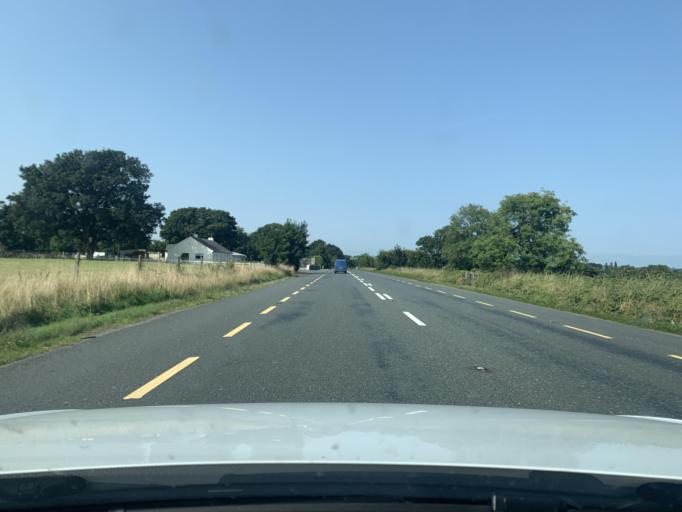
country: IE
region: Leinster
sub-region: An Iarmhi
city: Athlone
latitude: 53.5199
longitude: -8.0588
